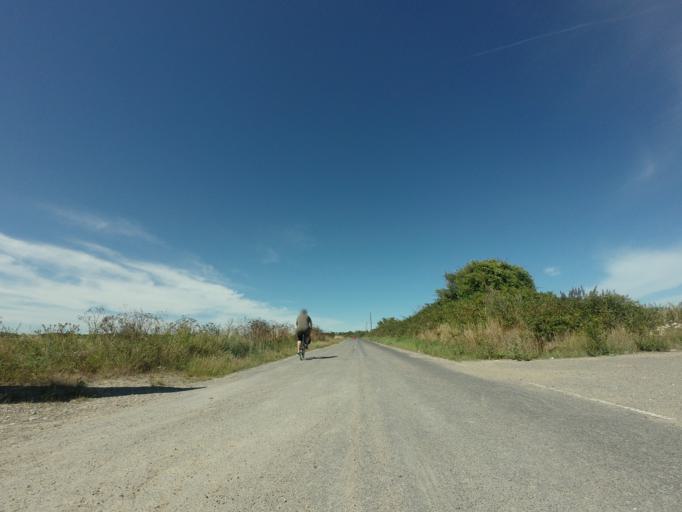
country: GB
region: England
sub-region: Kent
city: Sandwich
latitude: 51.3234
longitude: 1.3477
